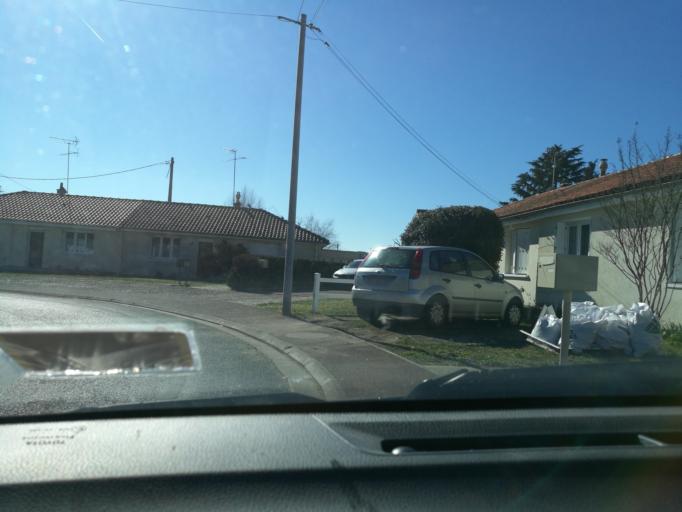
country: FR
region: Centre
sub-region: Departement du Loiret
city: Saint-Jean-de-la-Ruelle
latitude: 47.9015
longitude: 1.8650
